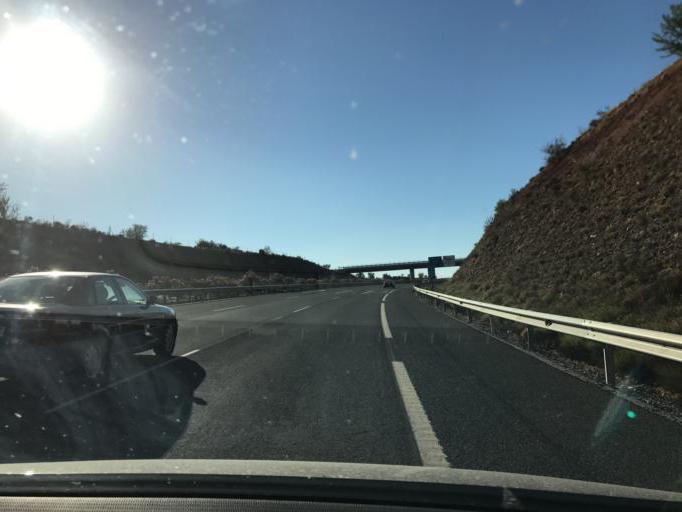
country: ES
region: Andalusia
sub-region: Provincia de Granada
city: Niguelas
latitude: 36.9644
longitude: -3.5539
